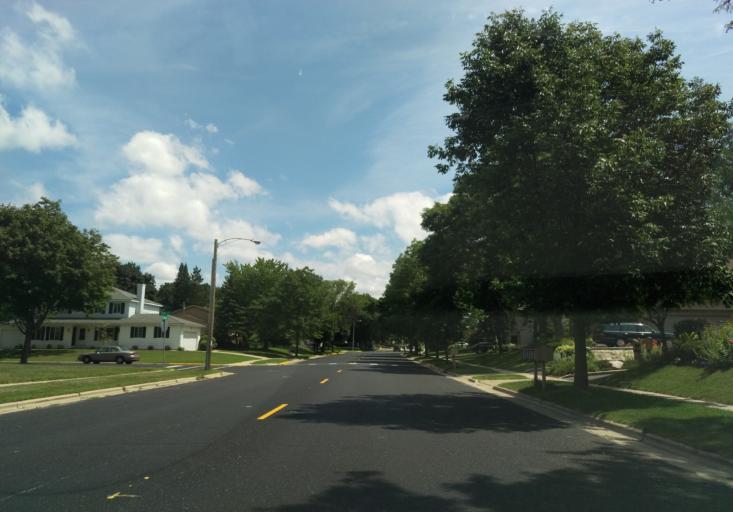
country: US
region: Wisconsin
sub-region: Dane County
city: Middleton
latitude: 43.1059
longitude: -89.5087
